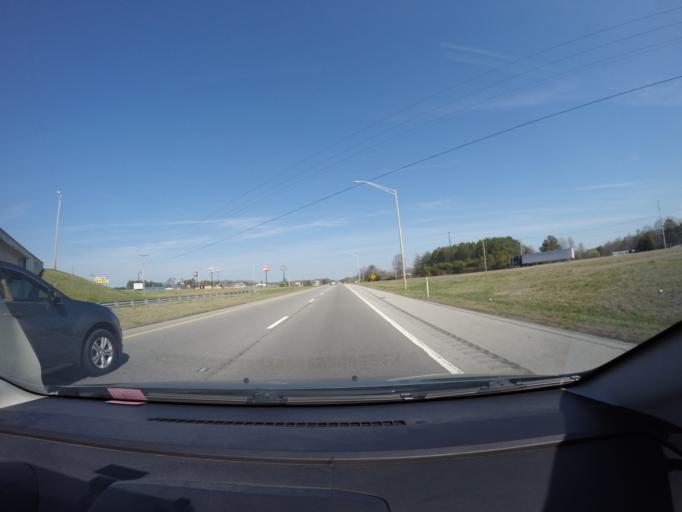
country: US
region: Tennessee
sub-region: Coffee County
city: Manchester
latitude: 35.4578
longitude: -86.0519
